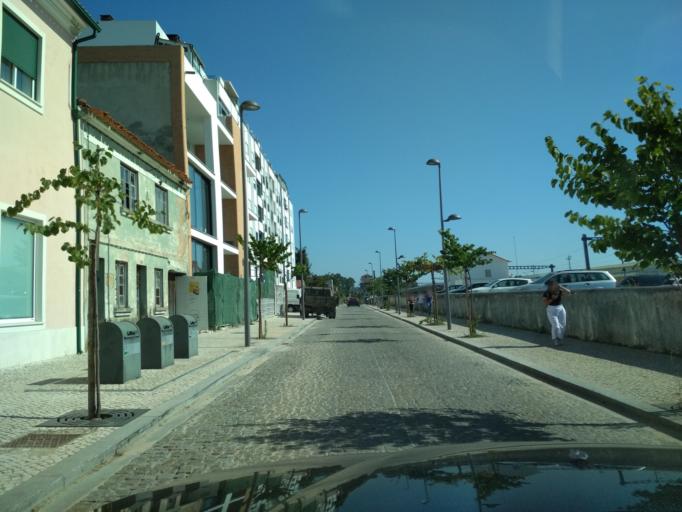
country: PT
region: Aveiro
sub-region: Mealhada
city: Mealhada
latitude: 40.3765
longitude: -8.4535
